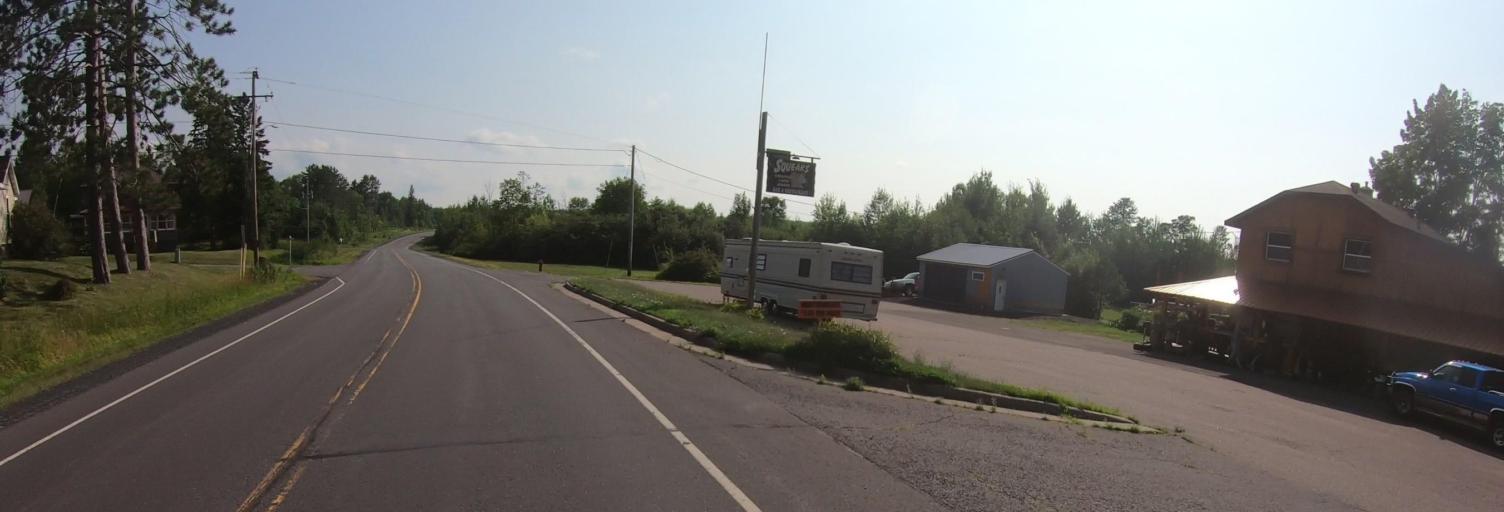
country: US
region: Wisconsin
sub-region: Iron County
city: Hurley
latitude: 46.4257
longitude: -90.2589
